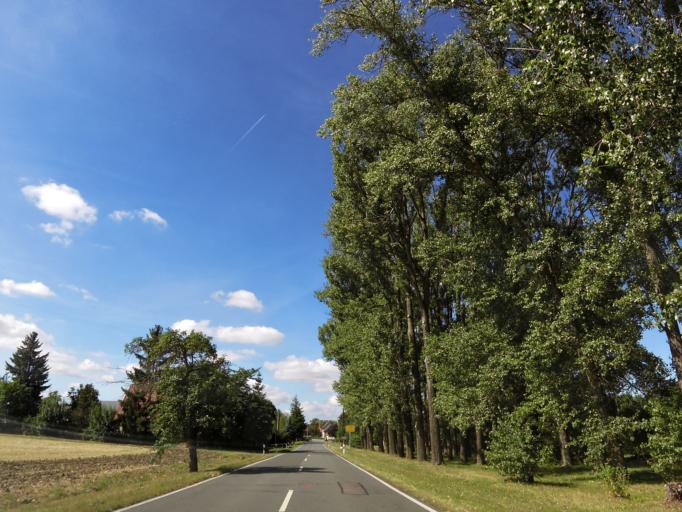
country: DE
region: Thuringia
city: Wandersleben
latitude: 50.9264
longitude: 10.8678
